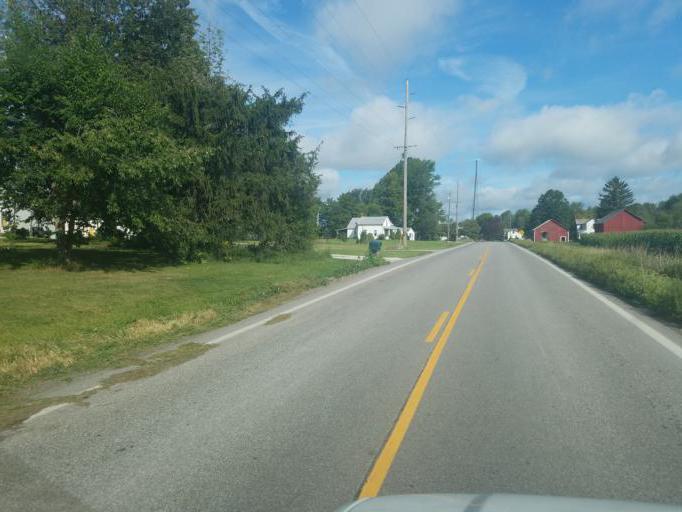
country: US
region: Ohio
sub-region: Wayne County
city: West Salem
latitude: 41.0218
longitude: -82.1227
